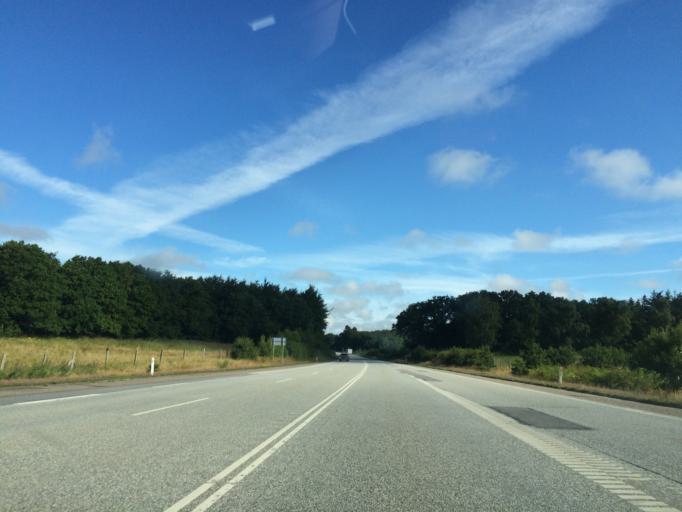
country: DK
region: Central Jutland
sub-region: Silkeborg Kommune
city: Kjellerup
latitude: 56.3453
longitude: 9.5327
